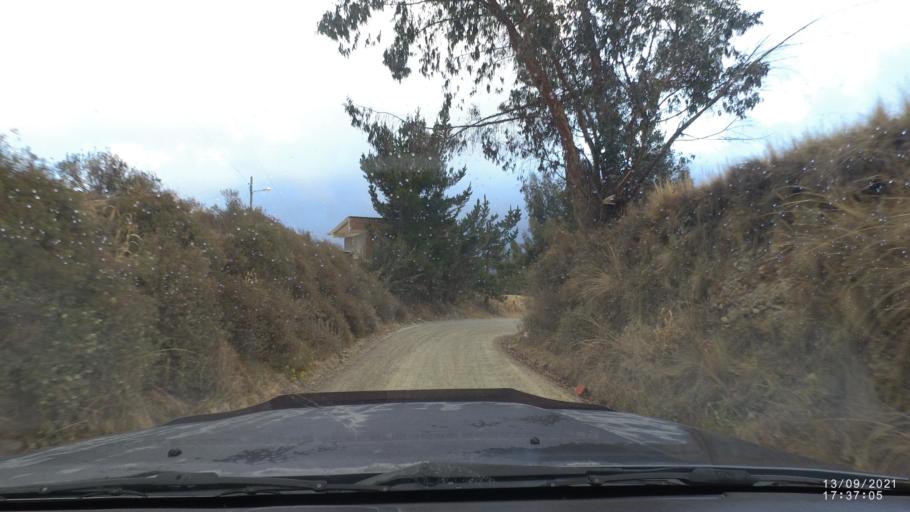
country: BO
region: Cochabamba
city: Colomi
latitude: -17.3620
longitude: -65.8035
